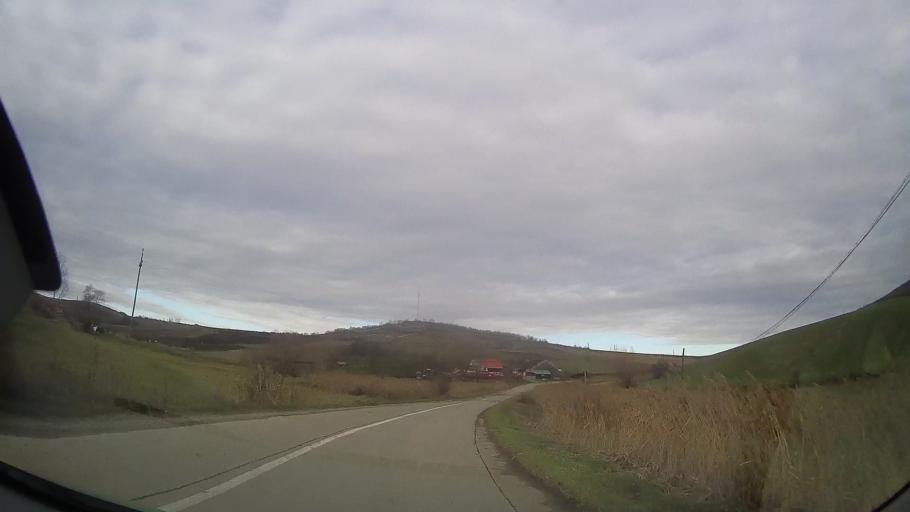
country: RO
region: Bistrita-Nasaud
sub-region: Comuna Micestii de Campie
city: Micestii de Campie
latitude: 46.8440
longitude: 24.3001
